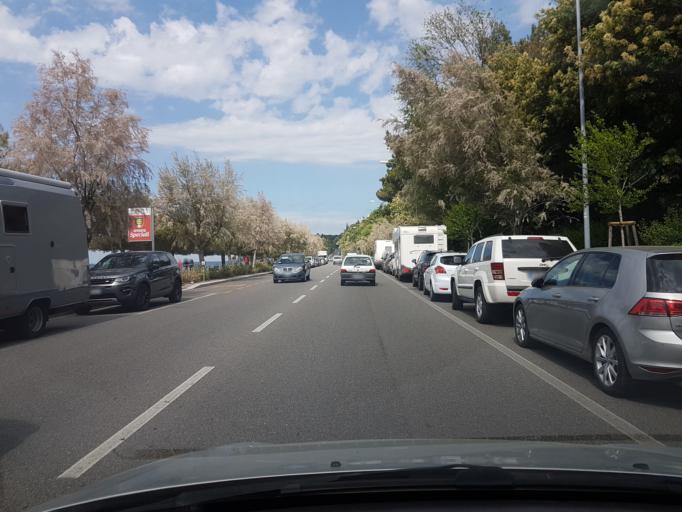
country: IT
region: Friuli Venezia Giulia
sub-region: Provincia di Trieste
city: Prosecco-Contovello
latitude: 45.6975
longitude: 13.7309
